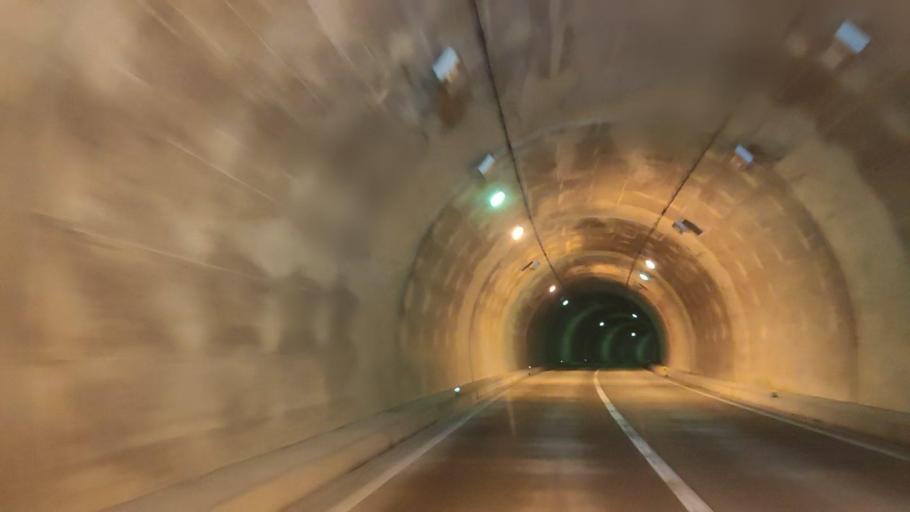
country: JP
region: Tottori
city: Tottori
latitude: 35.3464
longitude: 134.4607
